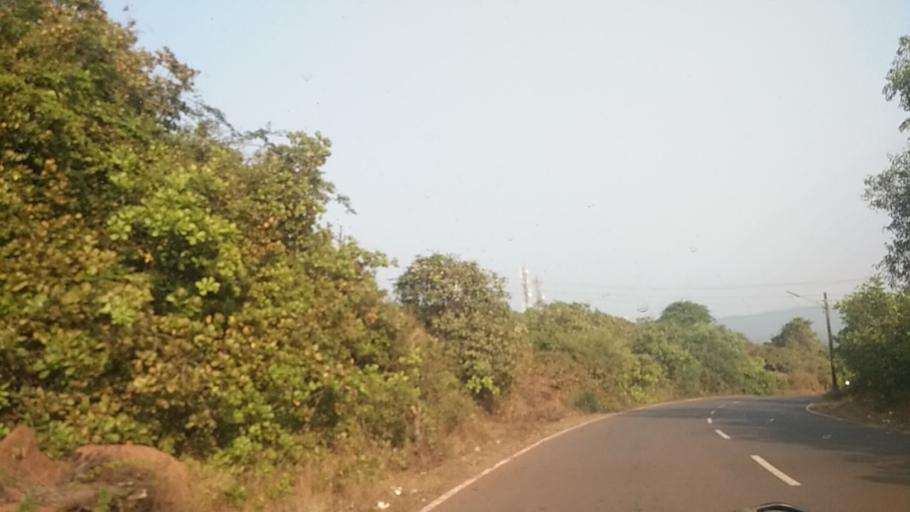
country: IN
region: Goa
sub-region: North Goa
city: Morjim
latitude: 15.6494
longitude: 73.7605
